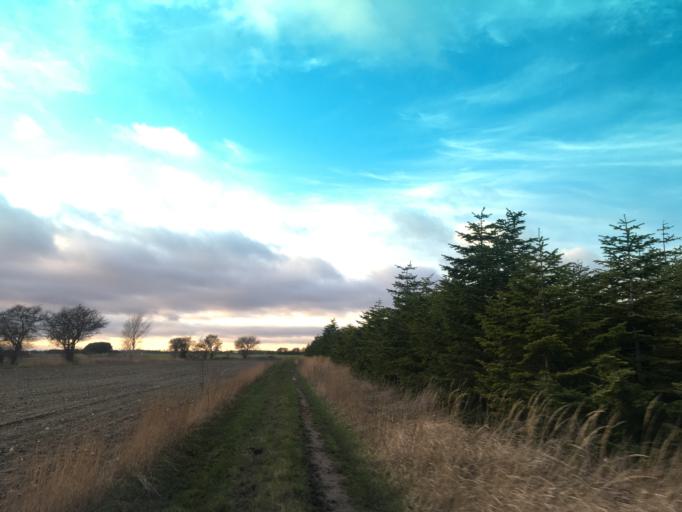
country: DK
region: Capital Region
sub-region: Dragor Kommune
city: Dragor
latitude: 55.5845
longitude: 12.6207
